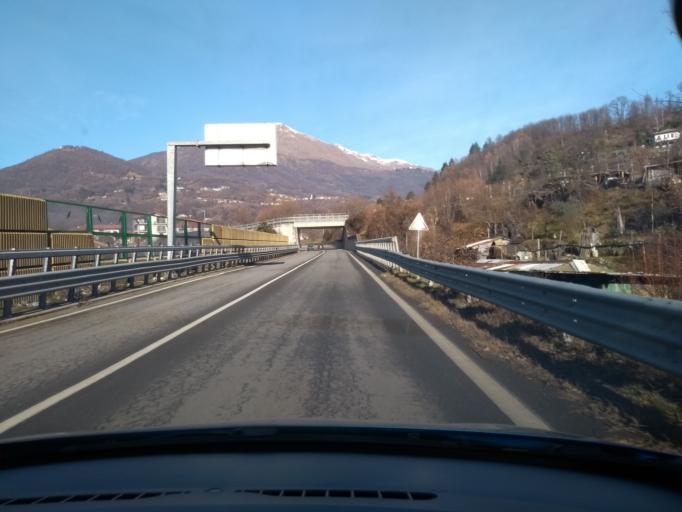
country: IT
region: Piedmont
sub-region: Provincia di Torino
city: Cuorgne
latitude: 45.3973
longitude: 7.6602
